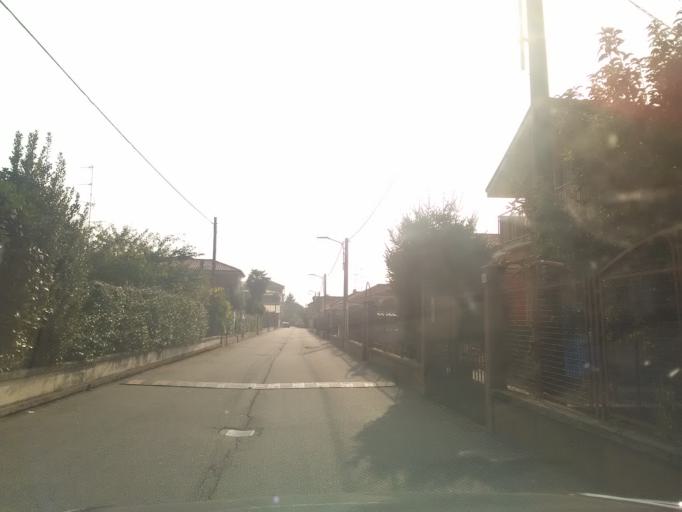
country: IT
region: Piedmont
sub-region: Provincia di Vercelli
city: Santhia
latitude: 45.3695
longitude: 8.1661
